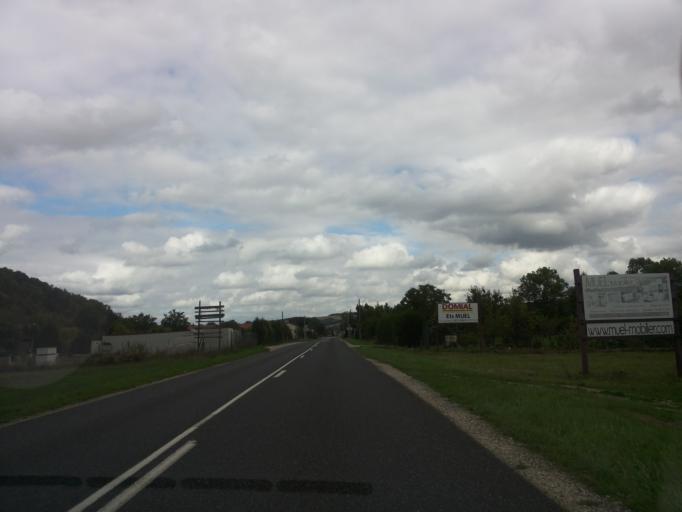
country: FR
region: Lorraine
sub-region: Departement de la Meuse
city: Ligny-en-Barrois
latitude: 48.6719
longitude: 5.3260
